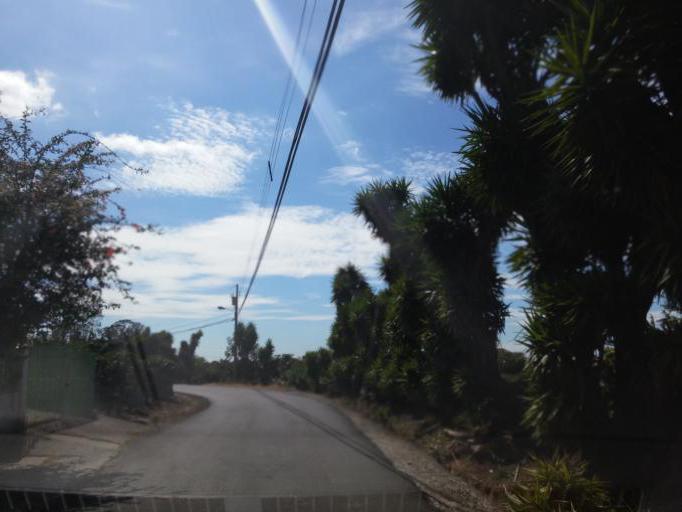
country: CR
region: Heredia
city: Santo Domingo
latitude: 10.0614
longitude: -84.1448
